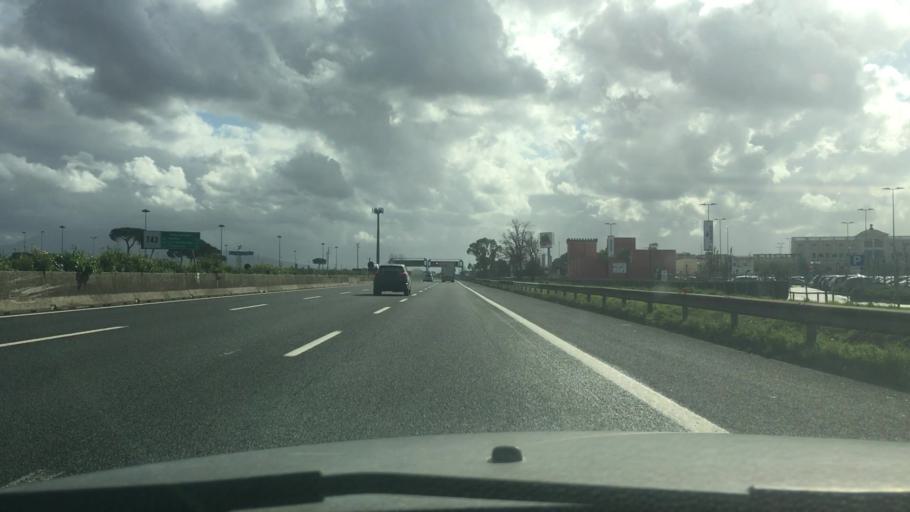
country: IT
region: Campania
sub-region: Provincia di Caserta
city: Marcianise
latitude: 41.0101
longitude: 14.3229
